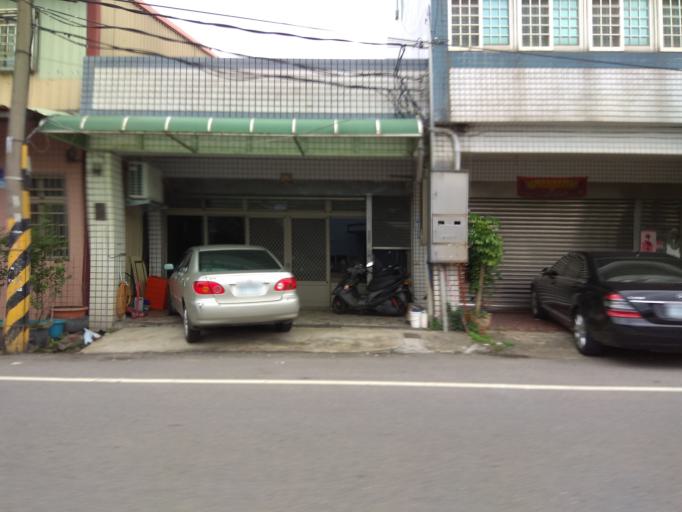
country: TW
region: Taiwan
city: Taoyuan City
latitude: 25.0476
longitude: 121.2231
